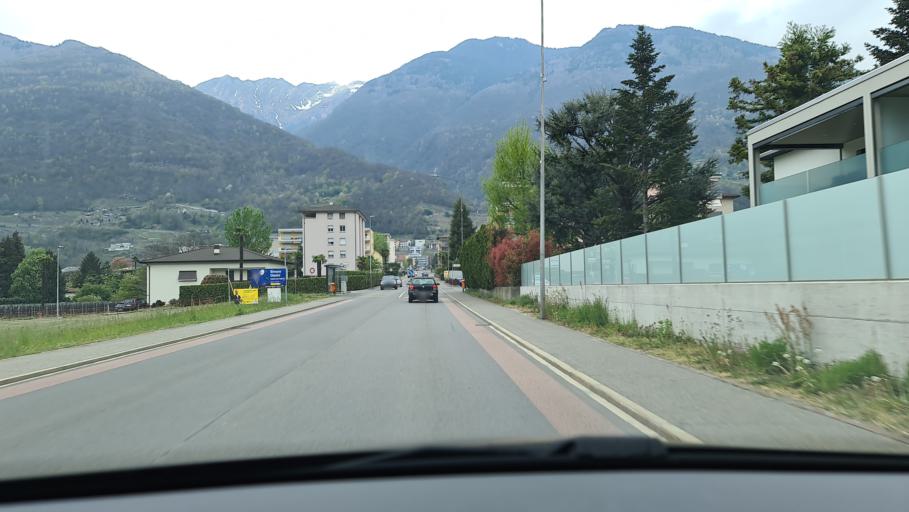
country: CH
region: Ticino
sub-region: Bellinzona District
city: Sementina
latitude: 46.1789
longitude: 8.9951
